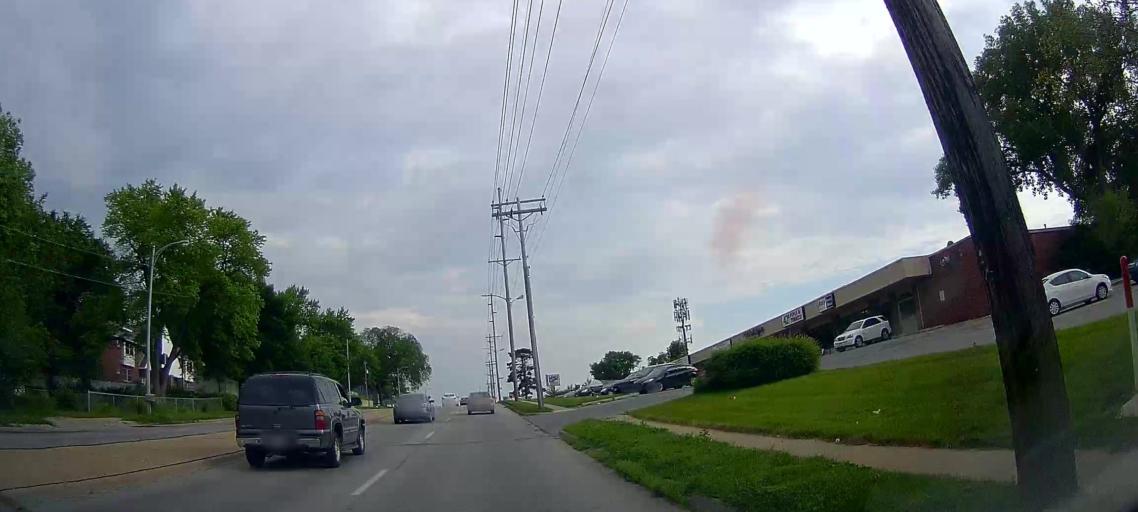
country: US
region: Nebraska
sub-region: Douglas County
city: Ralston
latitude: 41.2806
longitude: -96.0239
